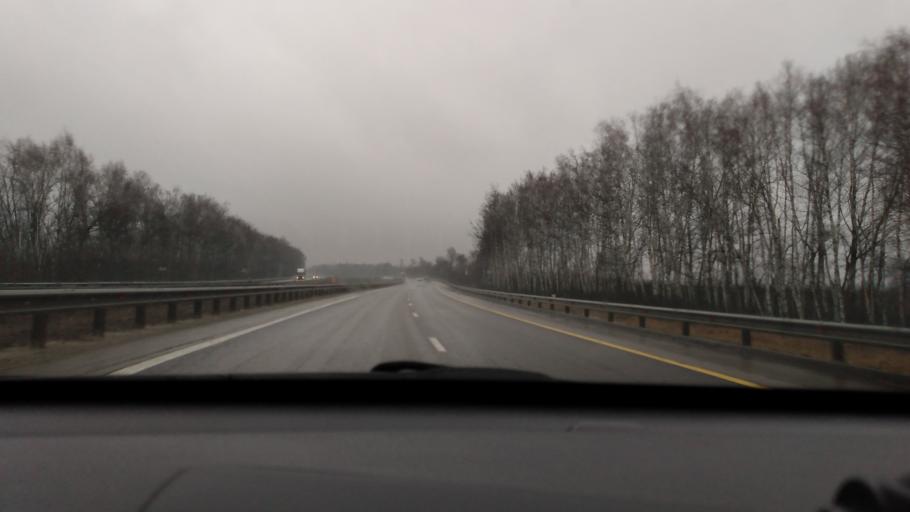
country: RU
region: Tula
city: Venev
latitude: 54.4673
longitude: 38.1739
